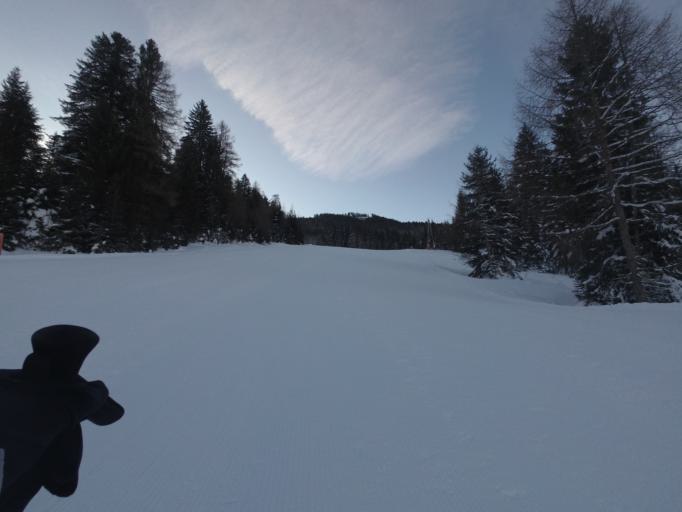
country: AT
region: Salzburg
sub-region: Politischer Bezirk Zell am See
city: Taxenbach
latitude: 47.2840
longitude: 13.0049
